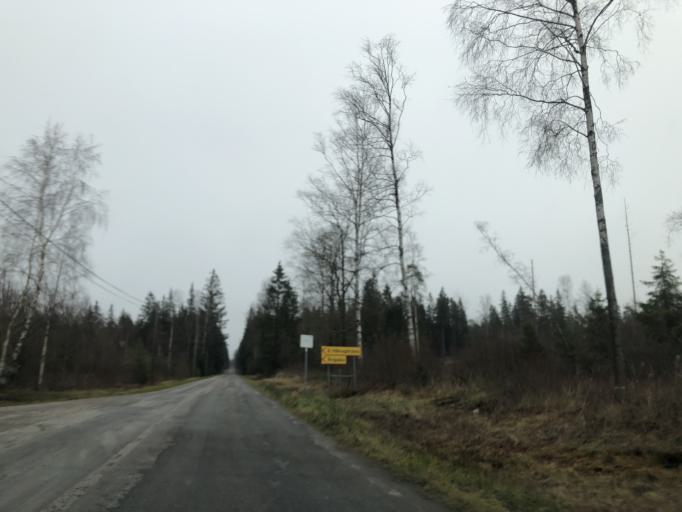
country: SE
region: Vaestra Goetaland
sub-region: Ulricehamns Kommun
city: Ulricehamn
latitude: 57.7054
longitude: 13.5037
